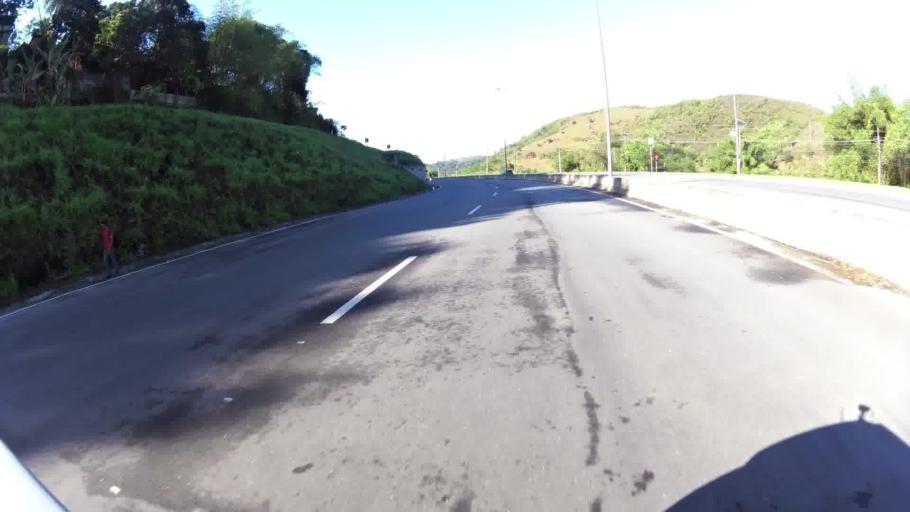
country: BR
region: Rio de Janeiro
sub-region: Petropolis
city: Petropolis
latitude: -22.6127
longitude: -43.2864
